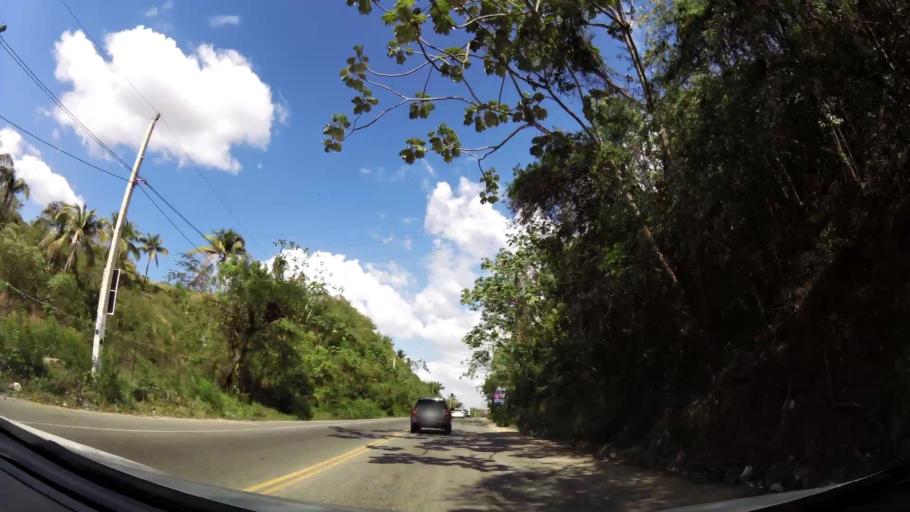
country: DO
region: San Cristobal
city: Bajos de Haina
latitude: 18.4274
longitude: -70.0524
